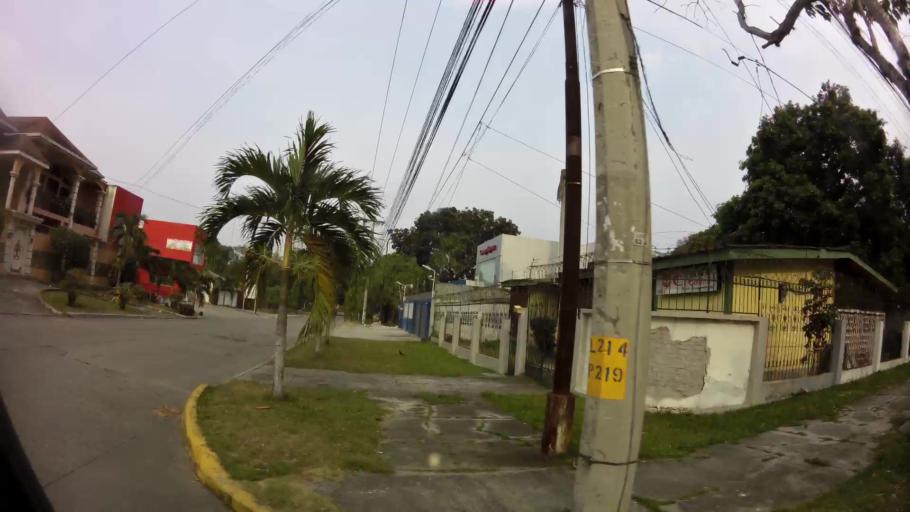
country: HN
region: Cortes
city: San Pedro Sula
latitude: 15.5141
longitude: -88.0311
